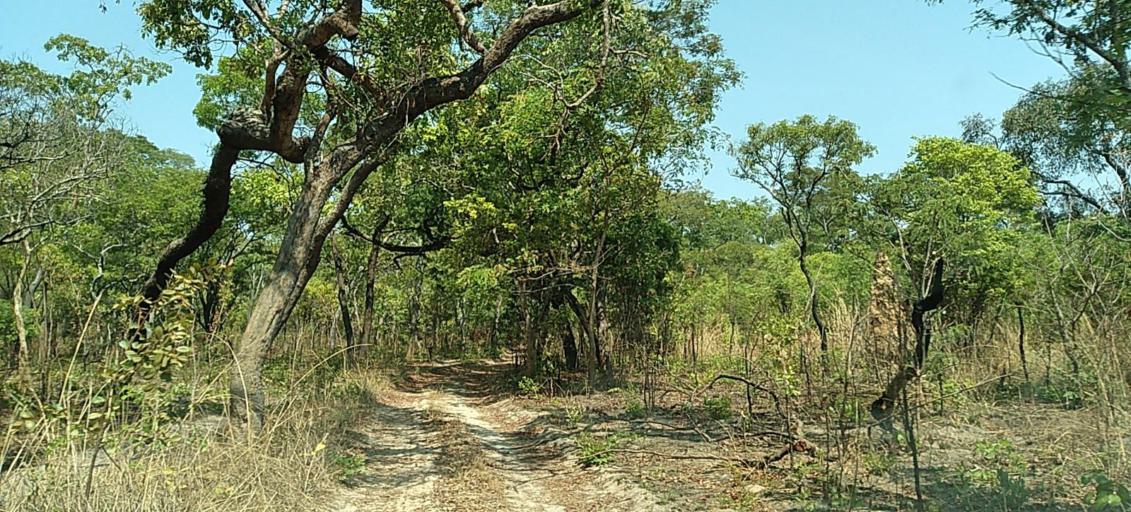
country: ZM
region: Copperbelt
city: Mpongwe
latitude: -13.7894
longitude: 28.0971
